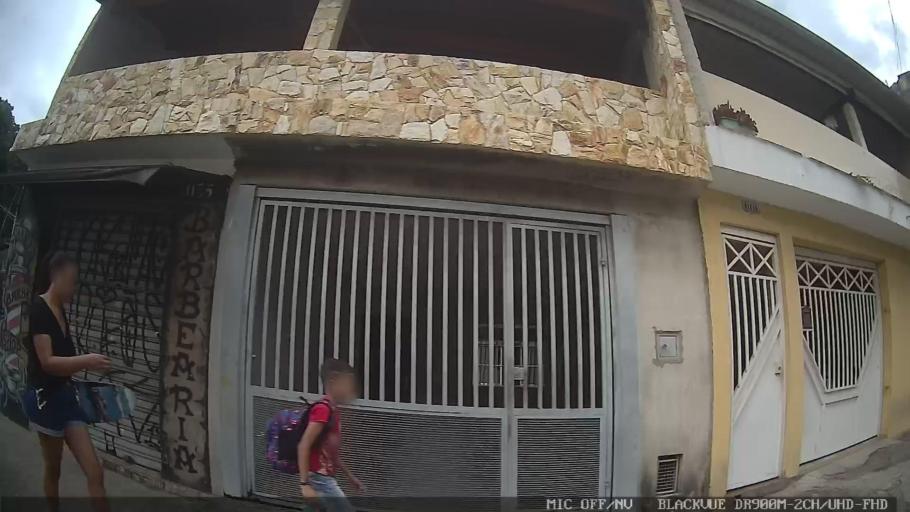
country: BR
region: Sao Paulo
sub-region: Ferraz De Vasconcelos
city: Ferraz de Vasconcelos
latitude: -23.5490
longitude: -46.3644
